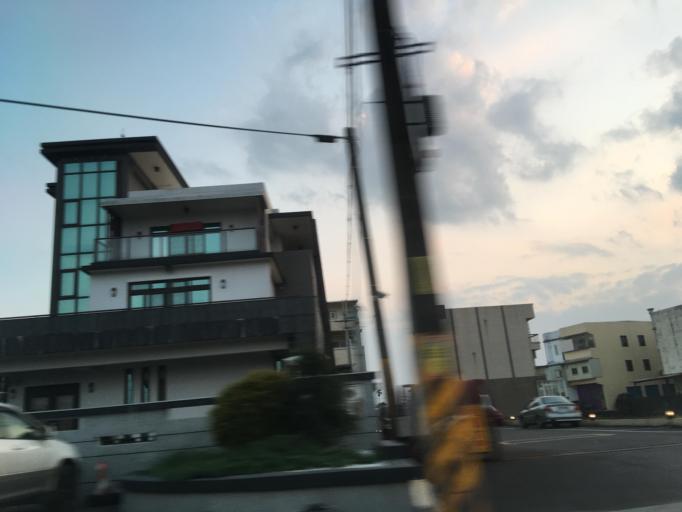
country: TW
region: Taiwan
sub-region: Yilan
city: Yilan
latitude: 24.6897
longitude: 121.7877
